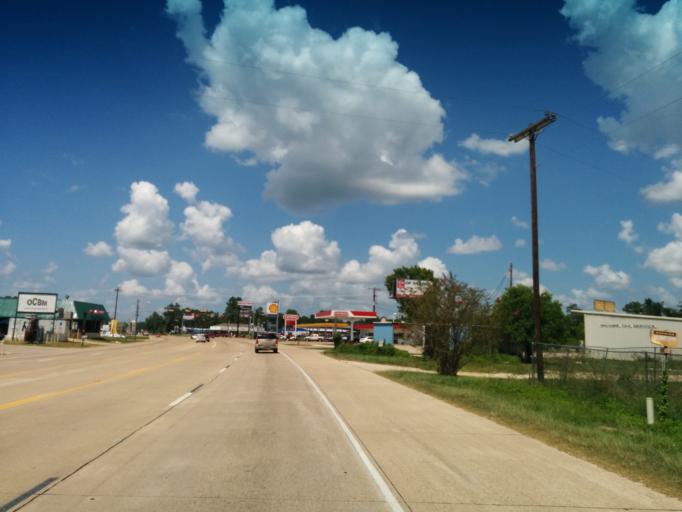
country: US
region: Texas
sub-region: Jasper County
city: Buna
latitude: 30.4404
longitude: -93.9699
